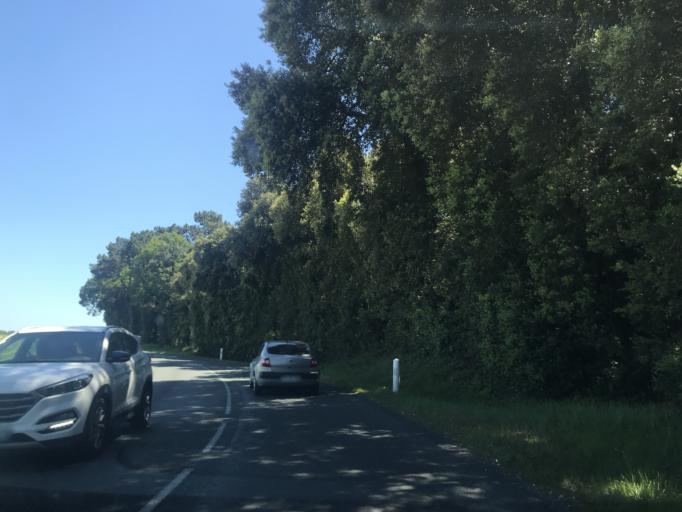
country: FR
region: Poitou-Charentes
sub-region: Departement de la Charente-Maritime
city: Meschers-sur-Gironde
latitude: 45.5910
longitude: -0.9650
